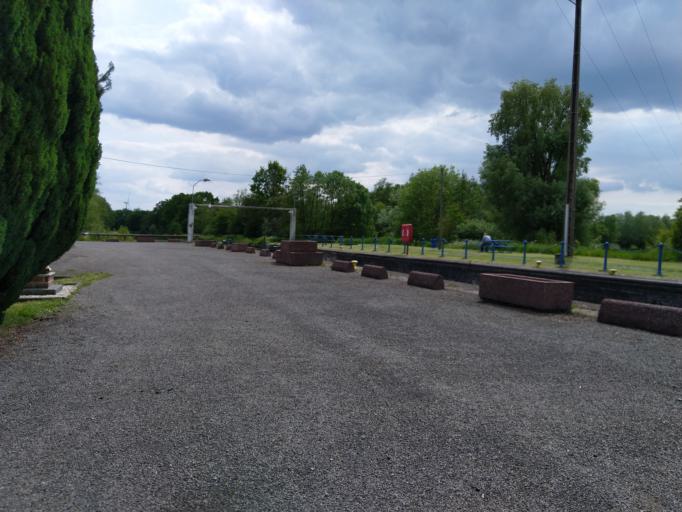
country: FR
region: Picardie
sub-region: Departement de l'Aisne
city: Wassigny
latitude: 50.0475
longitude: 3.6433
